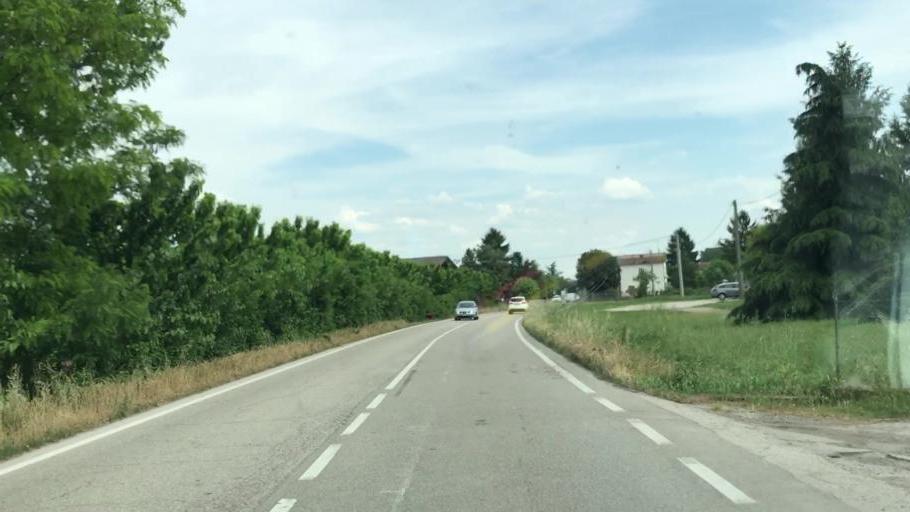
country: IT
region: Lombardy
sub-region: Provincia di Mantova
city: Bagnolo San Vito
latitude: 45.1208
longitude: 10.8982
